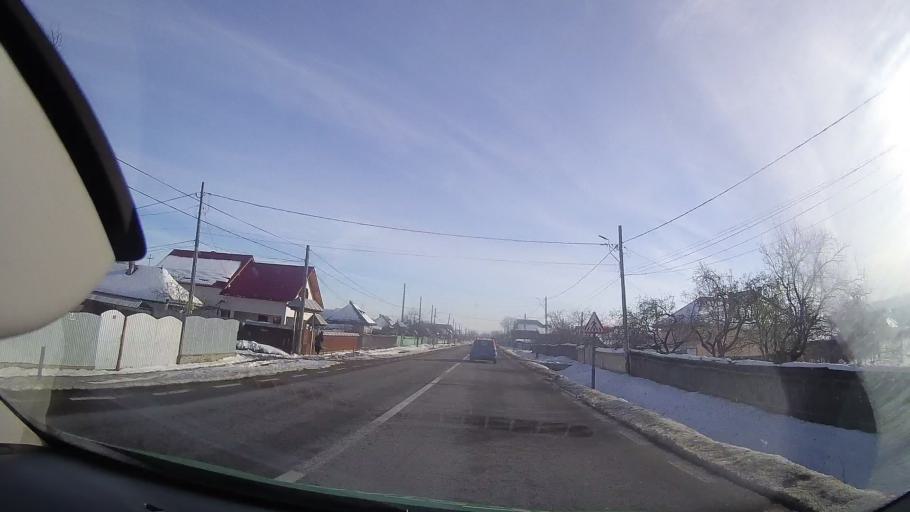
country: RO
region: Neamt
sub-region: Comuna Cracaoani
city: Cracaoani
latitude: 47.0945
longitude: 26.3171
